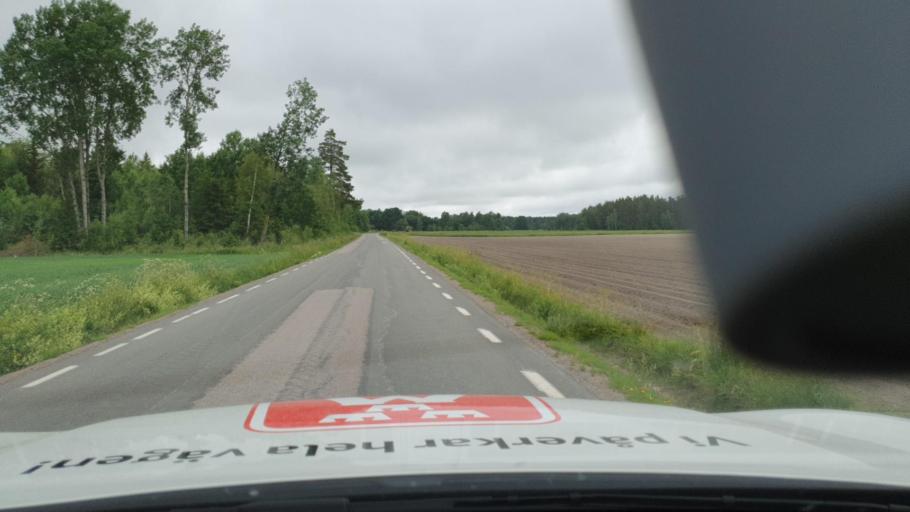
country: SE
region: Vaestra Goetaland
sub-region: Tibro Kommun
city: Tibro
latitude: 58.4004
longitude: 14.0646
